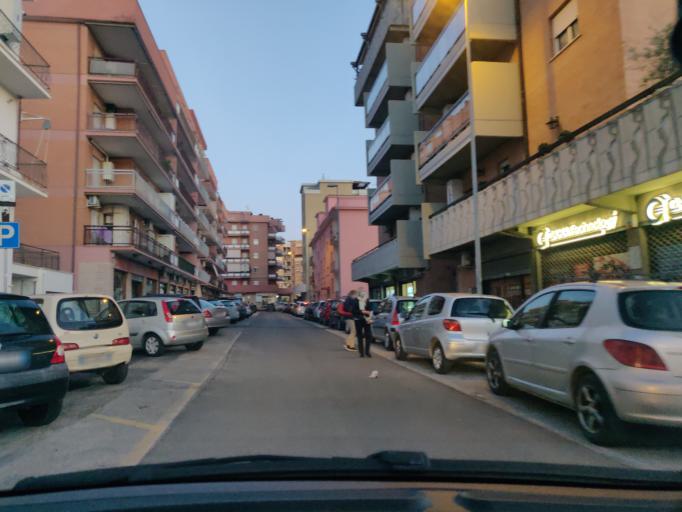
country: IT
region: Latium
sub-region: Citta metropolitana di Roma Capitale
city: Civitavecchia
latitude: 42.0888
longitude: 11.8015
